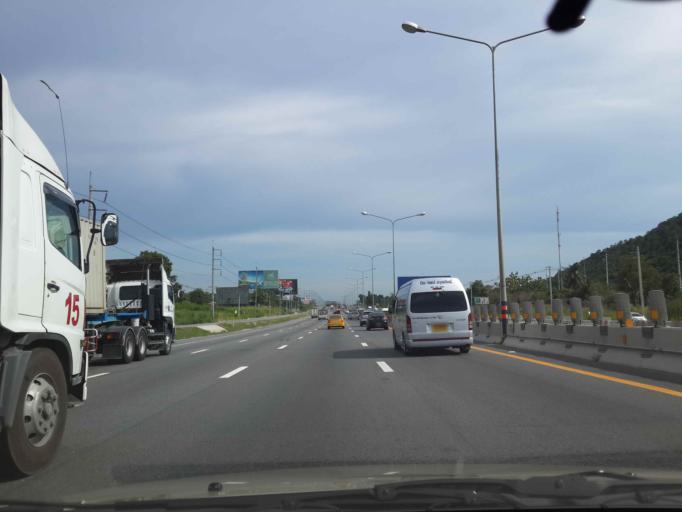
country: TH
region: Chon Buri
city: Chon Buri
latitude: 13.2759
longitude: 100.9906
